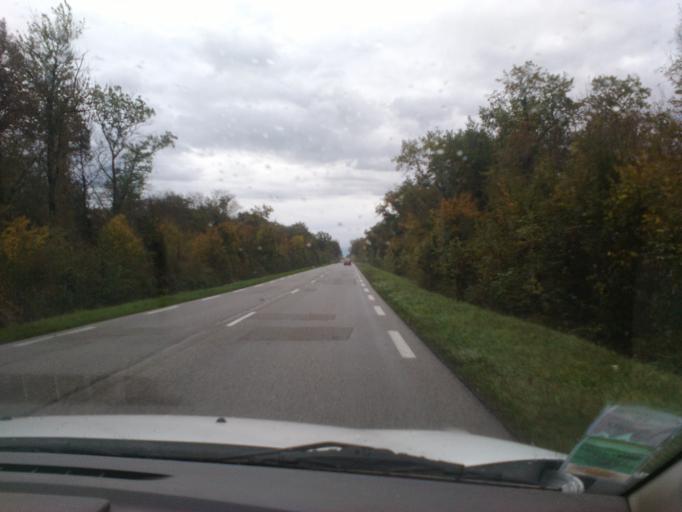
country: FR
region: Alsace
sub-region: Departement du Haut-Rhin
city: Widensolen
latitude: 48.0527
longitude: 7.4500
